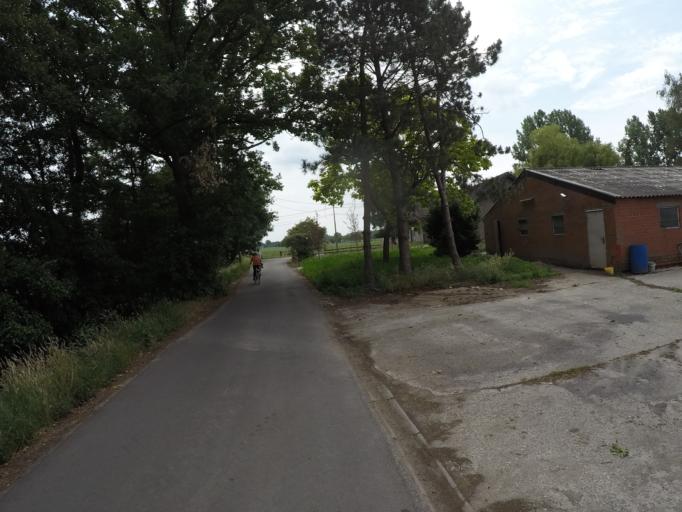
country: BE
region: Flanders
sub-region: Provincie Antwerpen
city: Essen
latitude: 51.4442
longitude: 4.5162
